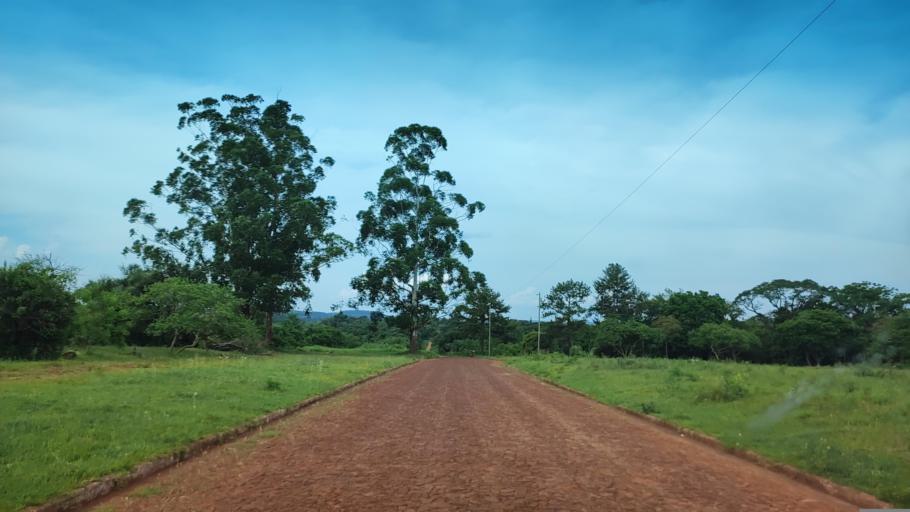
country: AR
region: Misiones
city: Gobernador Roca
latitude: -27.1270
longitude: -55.5150
